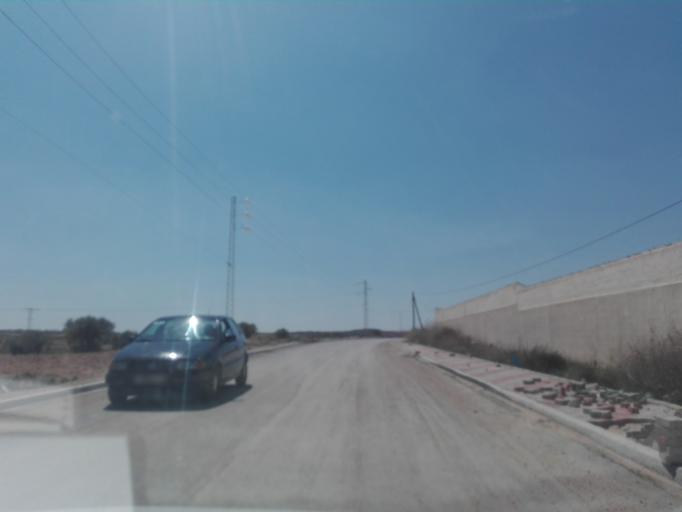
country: TN
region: Safaqis
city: Sfax
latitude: 34.7294
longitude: 10.5237
